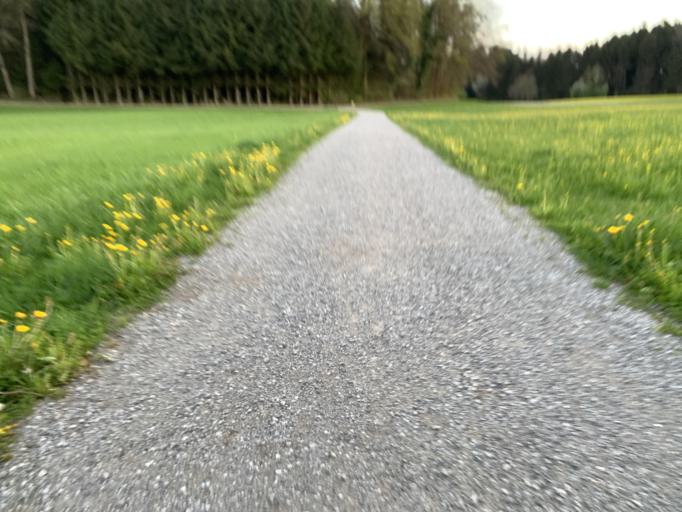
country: CH
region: Zurich
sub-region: Bezirk Hinwil
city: Hinwil
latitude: 47.2931
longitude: 8.8401
